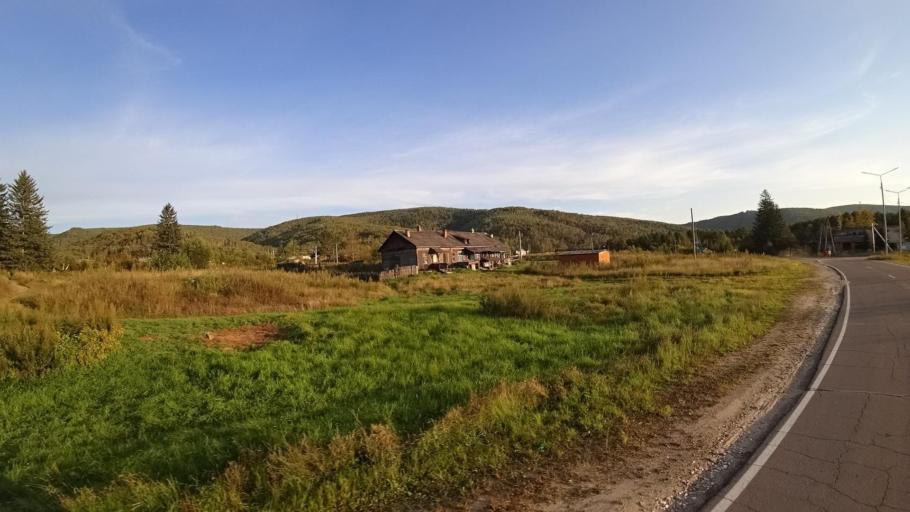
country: RU
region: Jewish Autonomous Oblast
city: Kul'dur
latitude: 49.1995
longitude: 131.6330
